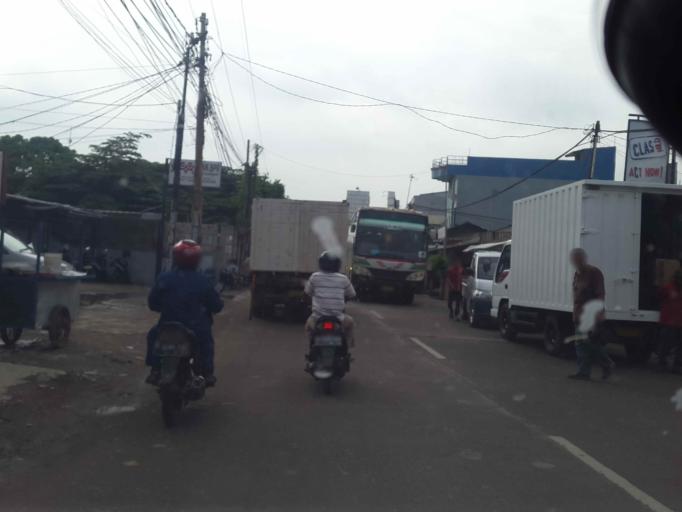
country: ID
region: West Java
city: Cikarang
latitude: -6.2607
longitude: 107.1471
